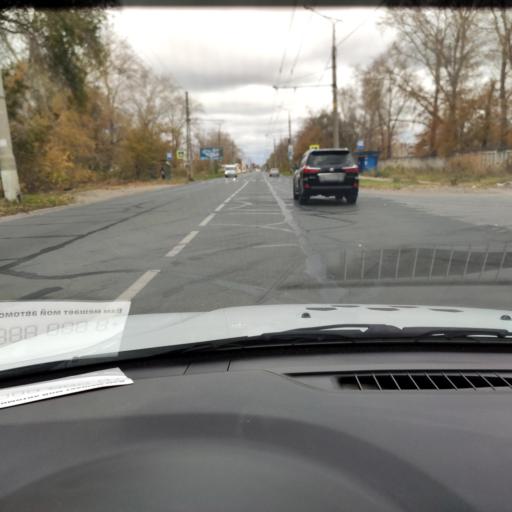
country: RU
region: Samara
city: Tol'yatti
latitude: 53.5276
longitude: 49.4363
